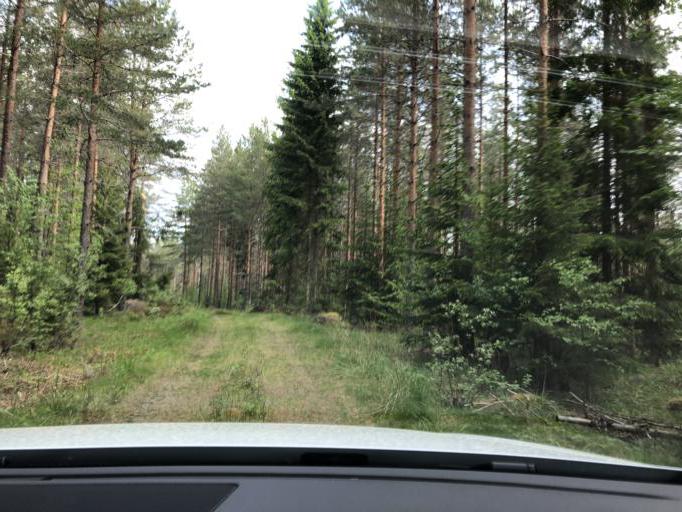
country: SE
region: Dalarna
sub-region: Avesta Kommun
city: Horndal
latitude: 60.2188
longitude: 16.5051
